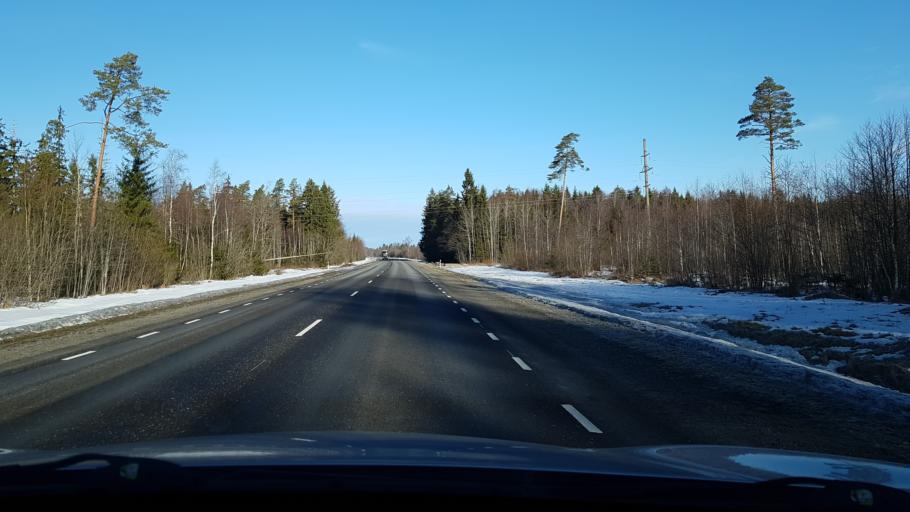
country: EE
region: Viljandimaa
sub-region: Vohma linn
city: Vohma
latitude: 58.6091
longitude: 25.5720
